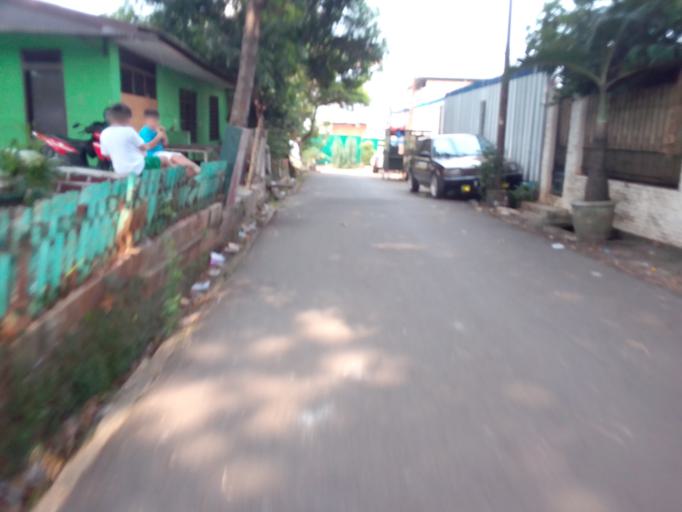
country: ID
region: Jakarta Raya
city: Jakarta
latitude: -6.2183
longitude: 106.7935
